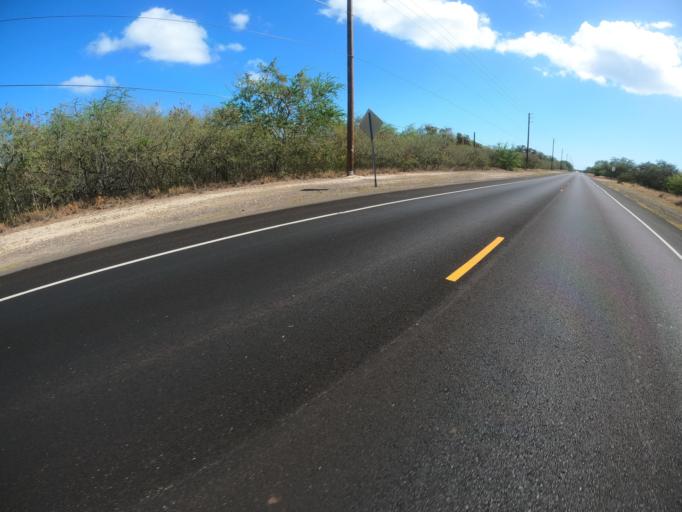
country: US
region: Hawaii
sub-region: Honolulu County
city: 'Ewa Villages
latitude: 21.3248
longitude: -158.0556
